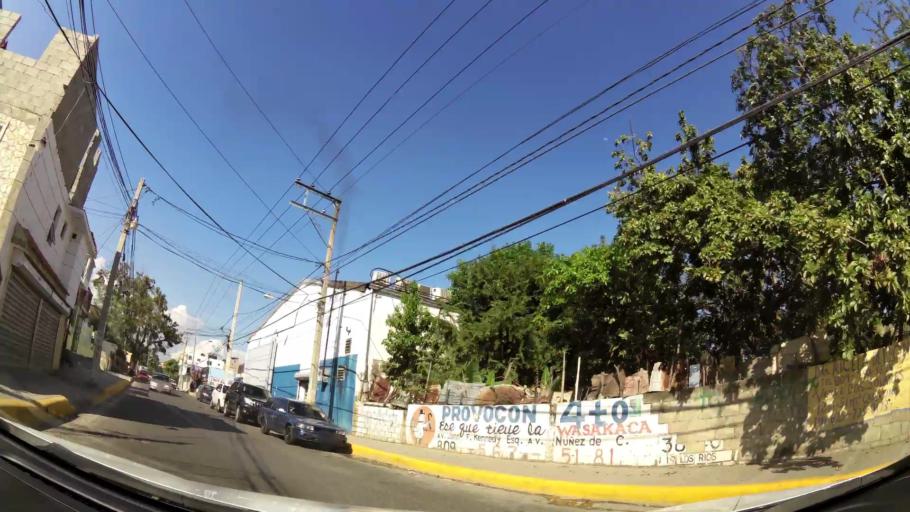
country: DO
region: Nacional
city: Santo Domingo
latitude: 18.4707
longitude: -69.9930
